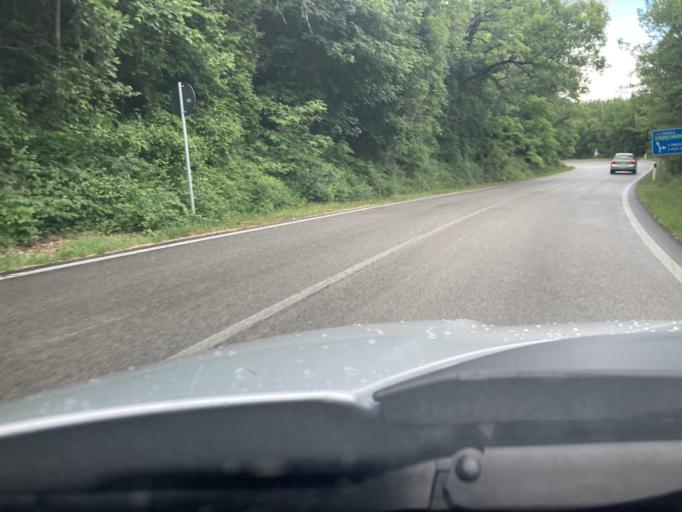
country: IT
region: Abruzzo
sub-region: Provincia dell' Aquila
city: San Panfilo d'Ocre
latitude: 42.2797
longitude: 13.4595
